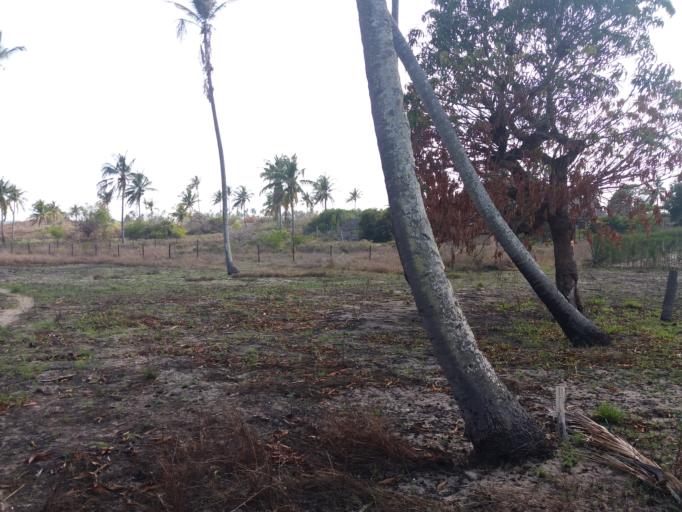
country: MZ
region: Inhambane
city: Inhambane
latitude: -23.9249
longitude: 35.3903
